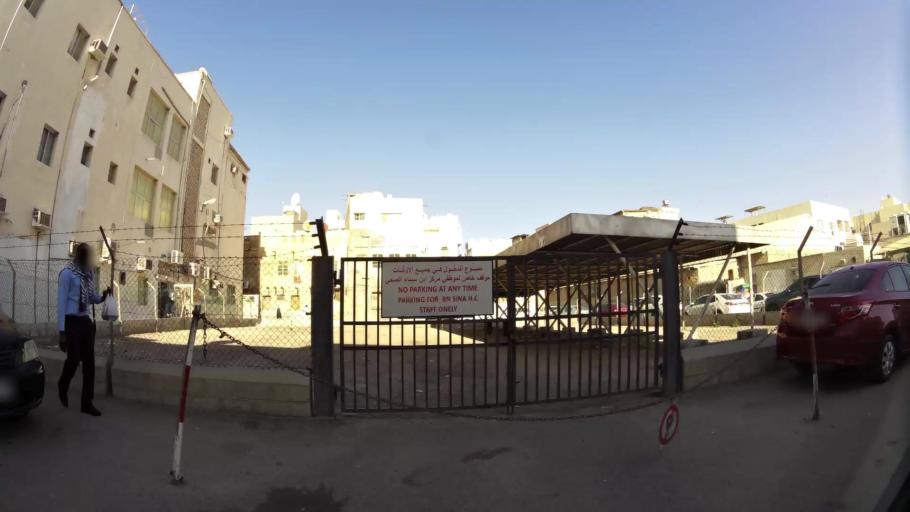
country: BH
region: Manama
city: Manama
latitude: 26.2359
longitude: 50.5835
